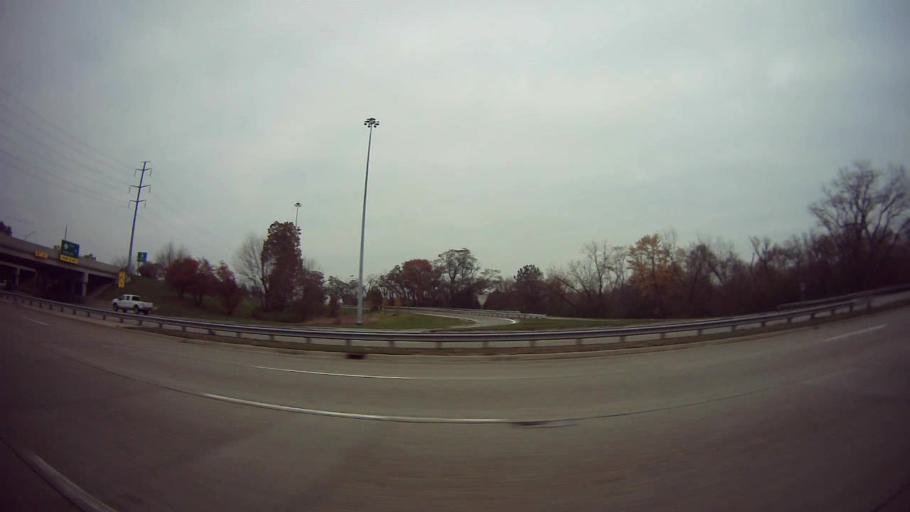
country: US
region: Michigan
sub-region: Wayne County
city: Redford
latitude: 42.4422
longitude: -83.2788
